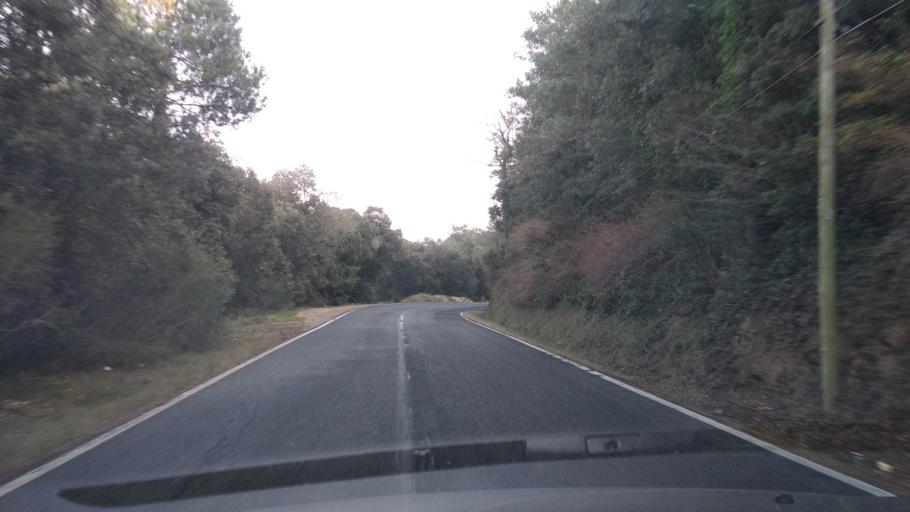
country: ES
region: Catalonia
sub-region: Provincia de Tarragona
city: Alforja
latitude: 41.2230
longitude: 0.9276
